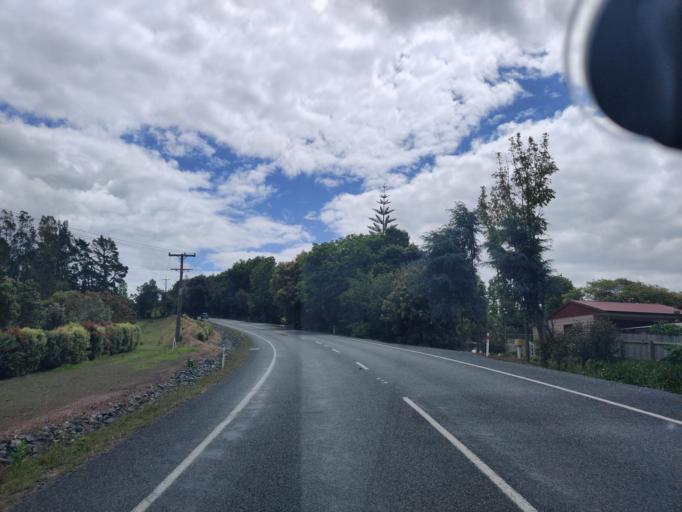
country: NZ
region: Northland
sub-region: Far North District
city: Paihia
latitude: -35.2908
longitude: 174.0135
